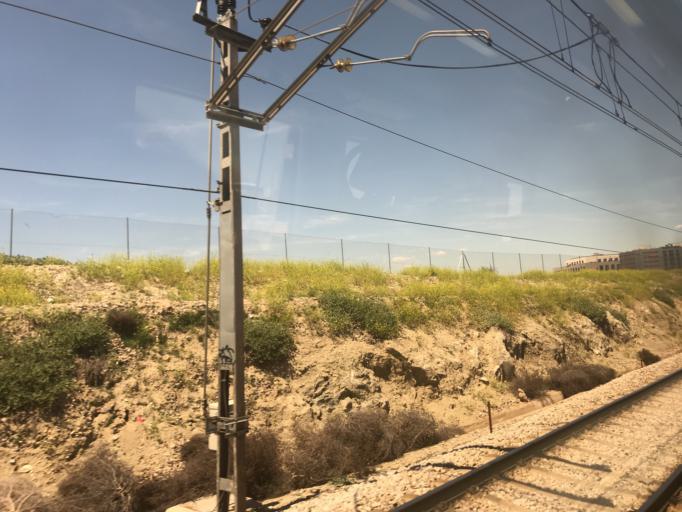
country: ES
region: Madrid
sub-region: Provincia de Madrid
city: Villaverde
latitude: 40.3284
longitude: -3.7059
